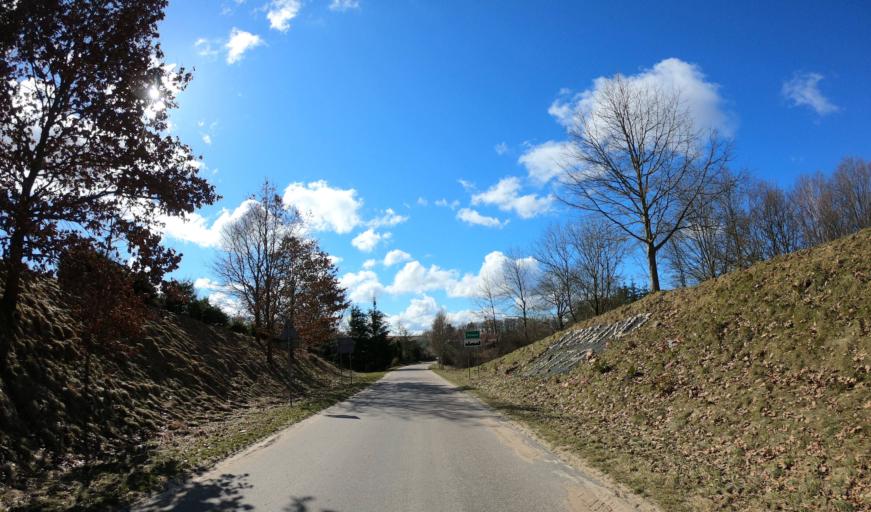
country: PL
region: West Pomeranian Voivodeship
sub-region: Powiat drawski
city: Zlocieniec
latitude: 53.4780
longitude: 15.9799
